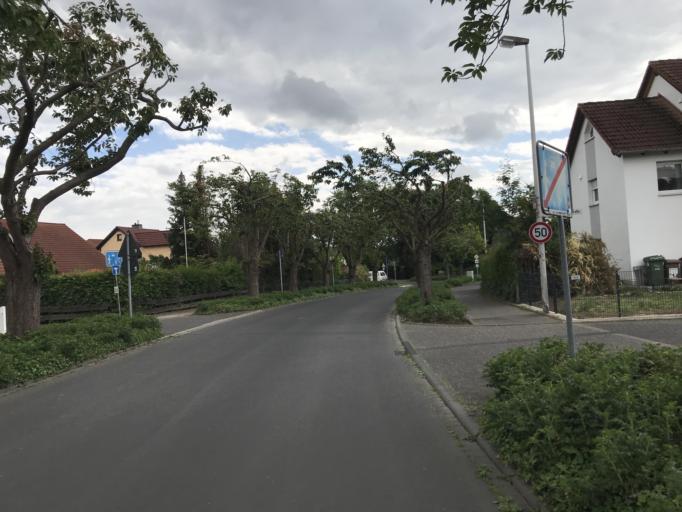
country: DE
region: Hesse
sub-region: Regierungsbezirk Kassel
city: Baunatal
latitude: 51.2502
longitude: 9.4042
